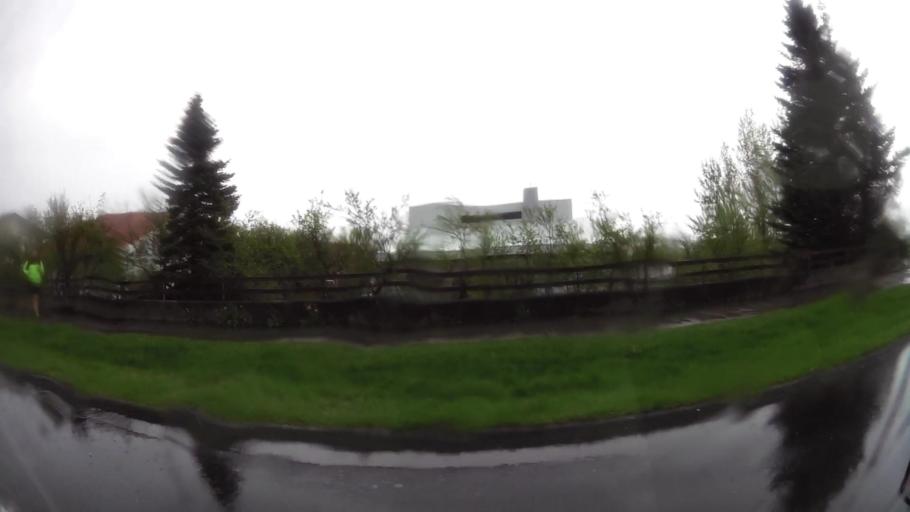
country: IS
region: Capital Region
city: Reykjavik
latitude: 64.1061
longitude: -21.8073
